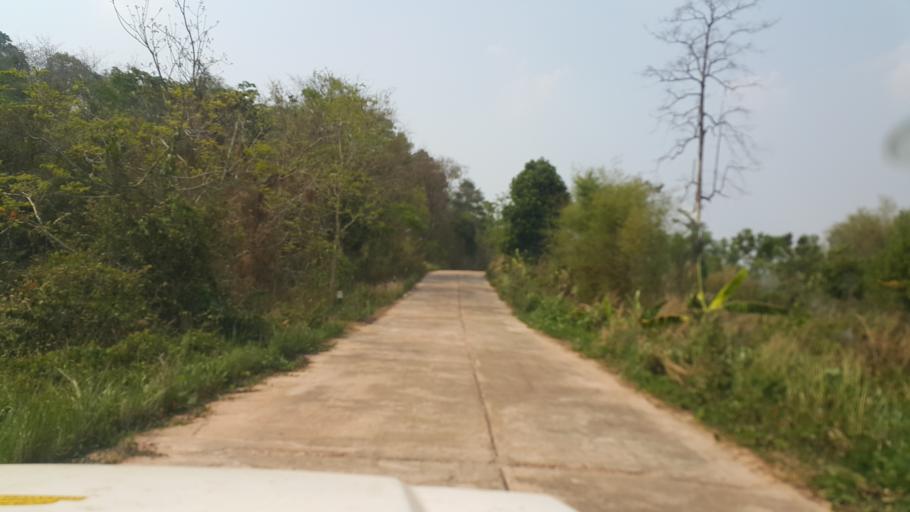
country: TH
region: Nakhon Phanom
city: Ban Phaeng
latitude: 17.9562
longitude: 104.1586
